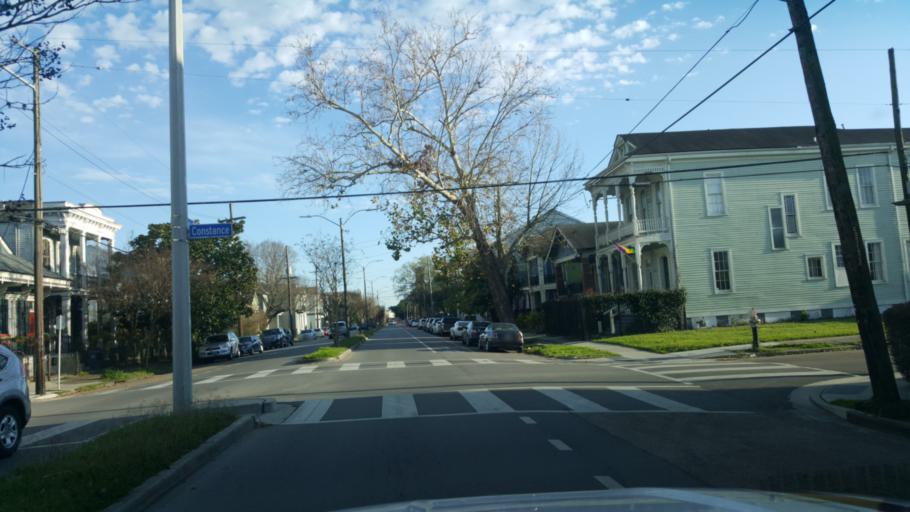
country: US
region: Louisiana
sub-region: Jefferson Parish
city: Harvey
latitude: 29.9290
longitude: -90.0763
